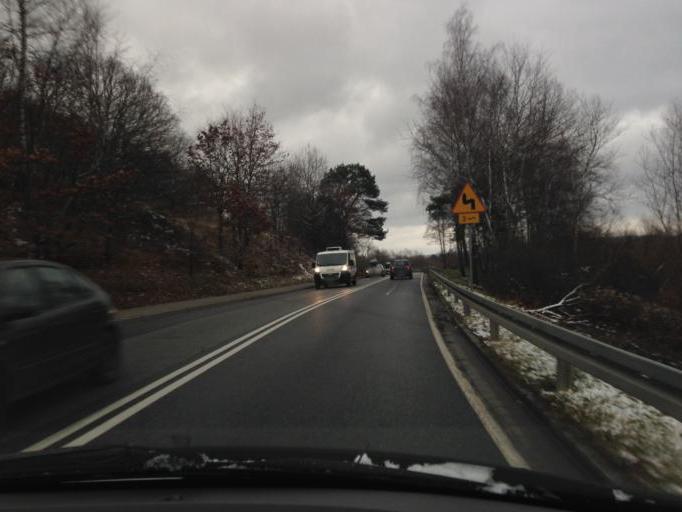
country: PL
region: Lesser Poland Voivodeship
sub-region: Powiat tarnowski
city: Zakliczyn
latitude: 49.8690
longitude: 20.7826
